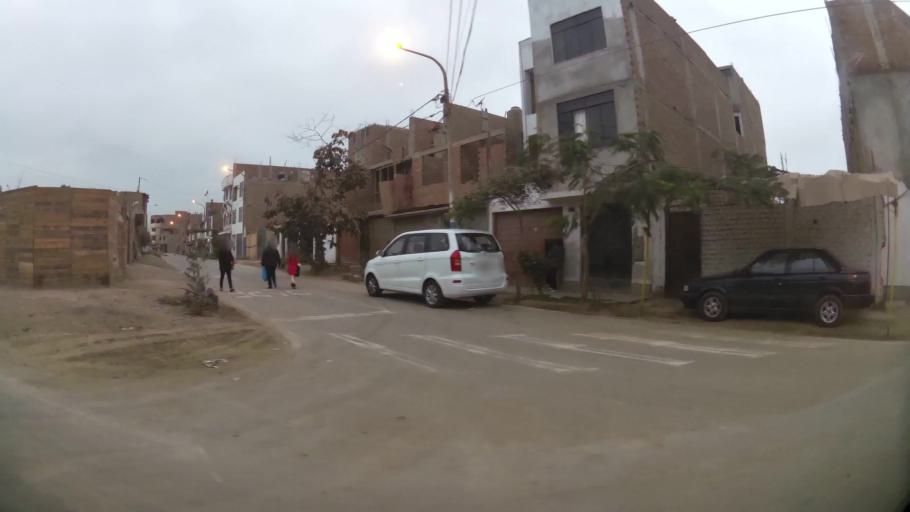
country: PE
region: Lima
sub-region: Lima
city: Independencia
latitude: -11.9802
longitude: -77.0989
